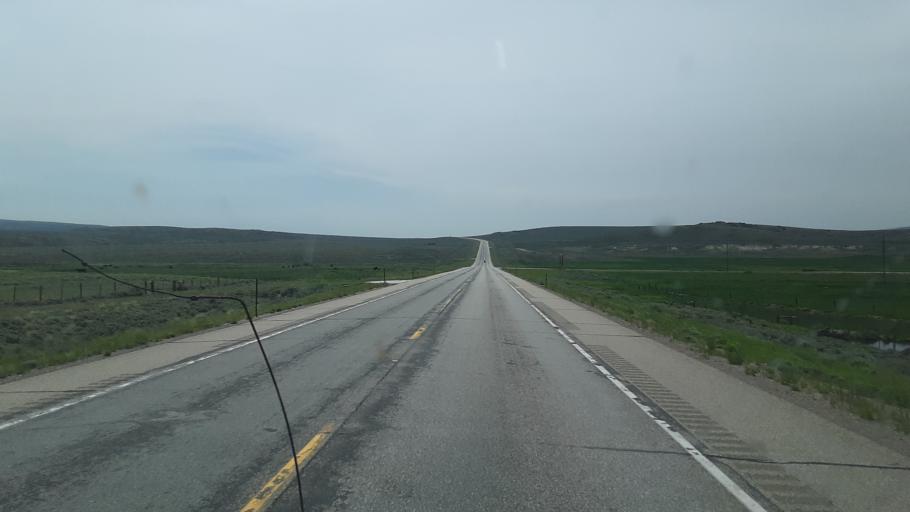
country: US
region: Wyoming
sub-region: Carbon County
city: Saratoga
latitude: 41.1185
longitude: -106.5355
